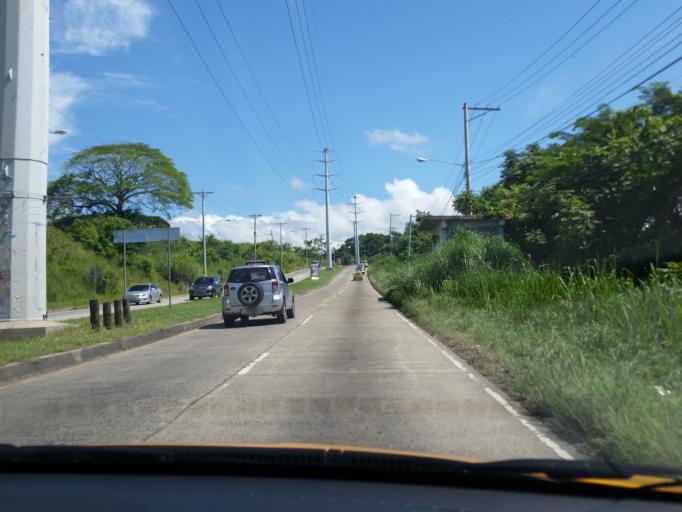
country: PA
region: Panama
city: San Miguelito
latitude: 9.0615
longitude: -79.4621
